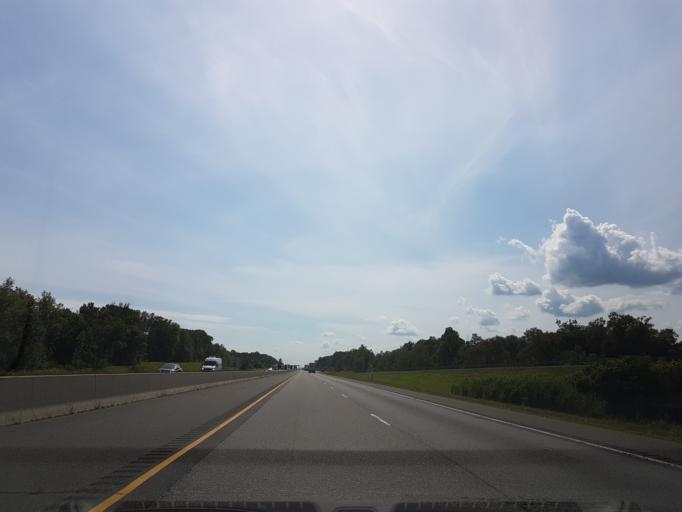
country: CA
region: Ontario
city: Prescott
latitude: 44.7464
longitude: -75.4905
